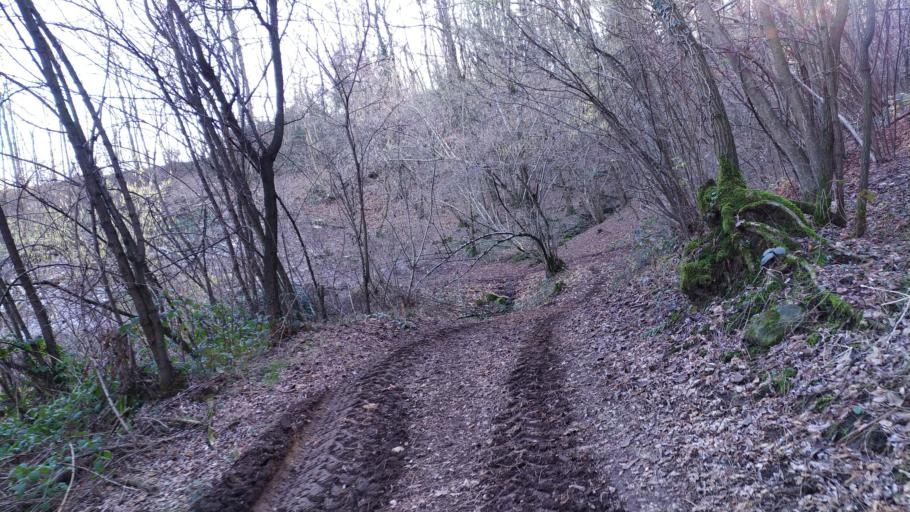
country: IT
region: Veneto
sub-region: Provincia di Vicenza
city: Monte di Malo
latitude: 45.6730
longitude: 11.3619
